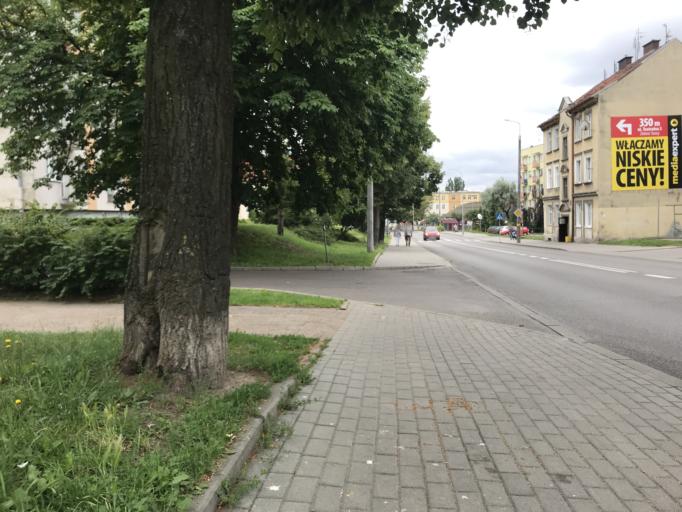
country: PL
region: Warmian-Masurian Voivodeship
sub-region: Powiat elblaski
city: Elblag
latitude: 54.1691
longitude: 19.4012
